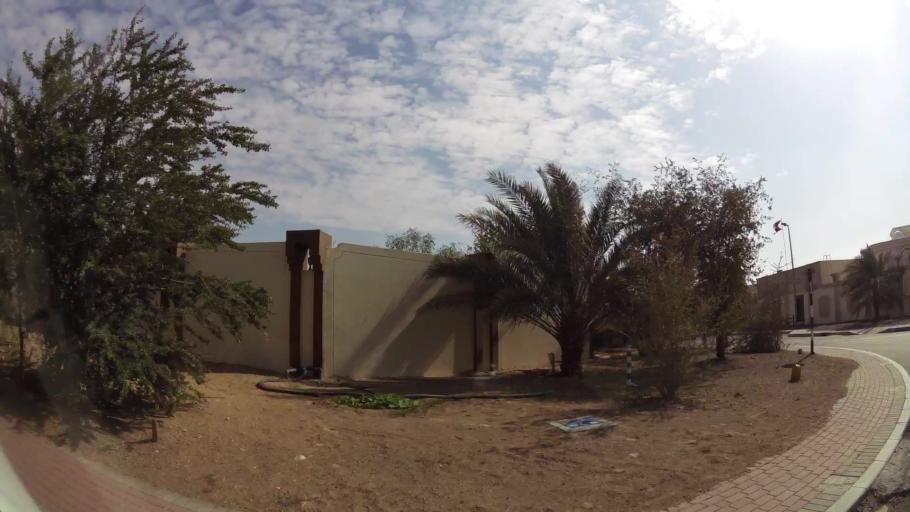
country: AE
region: Abu Dhabi
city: Al Ain
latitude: 24.1026
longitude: 55.9119
